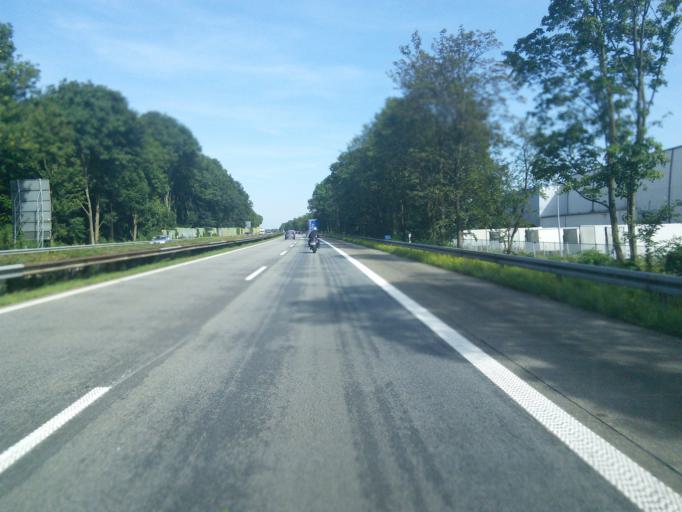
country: DE
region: North Rhine-Westphalia
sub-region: Regierungsbezirk Dusseldorf
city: Willich
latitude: 51.2355
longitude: 6.5234
